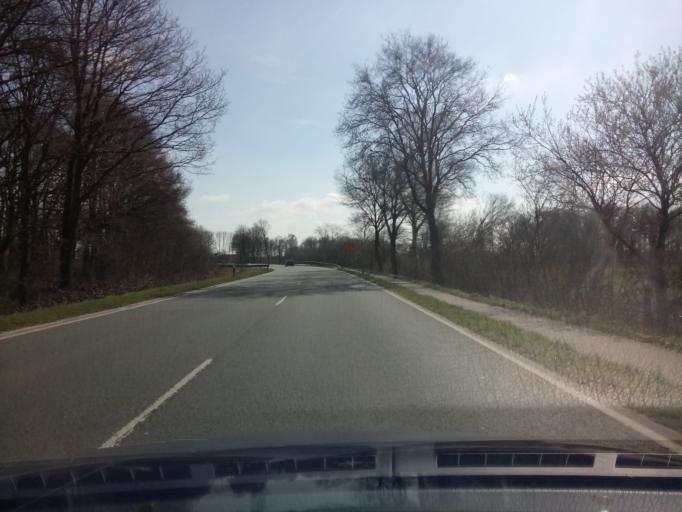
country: NL
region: Drenthe
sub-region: Gemeente Coevorden
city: Coevorden
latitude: 52.6392
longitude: 6.7582
